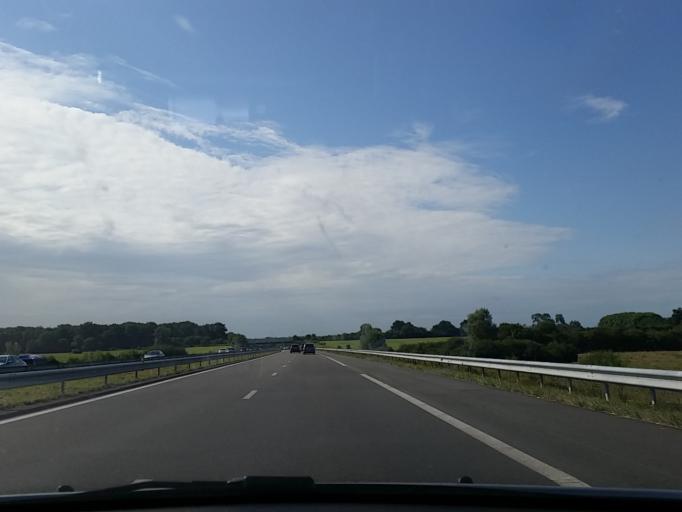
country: FR
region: Centre
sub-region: Departement du Cher
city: Orval
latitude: 46.8084
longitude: 2.4123
